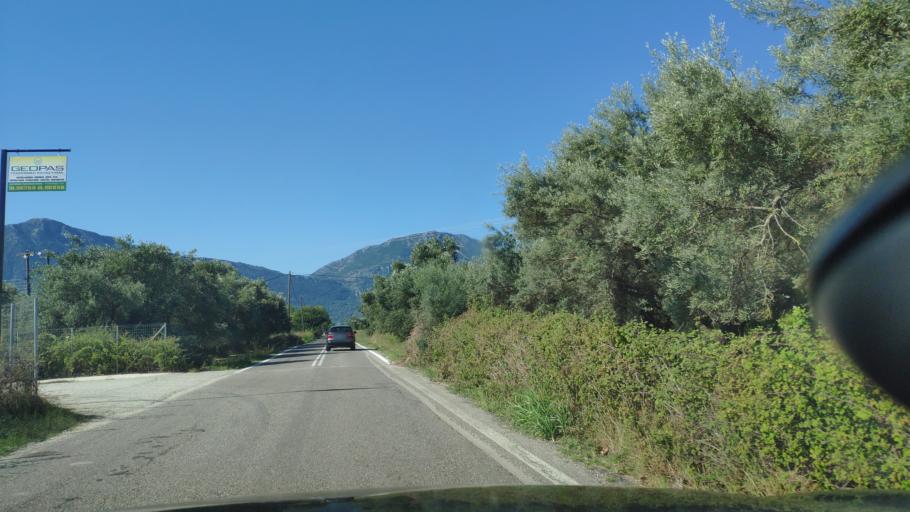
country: GR
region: West Greece
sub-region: Nomos Aitolias kai Akarnanias
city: Kandila
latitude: 38.6840
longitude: 20.9431
